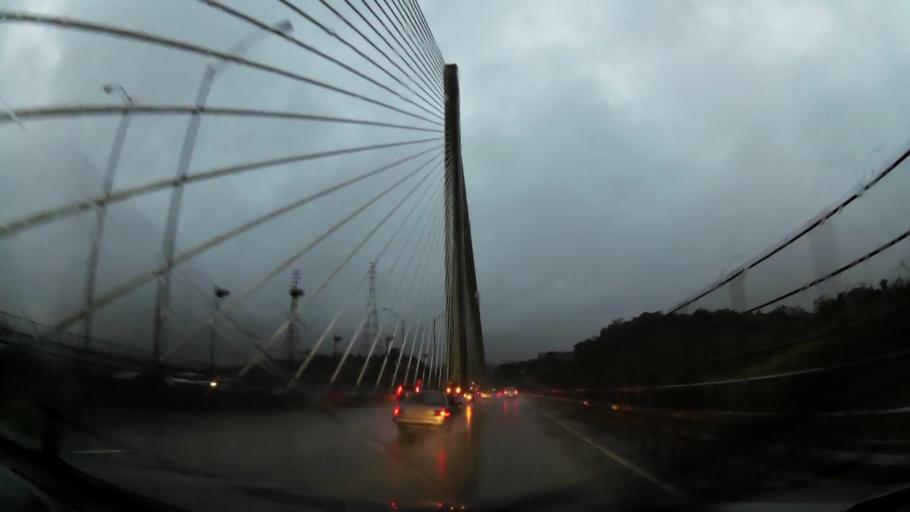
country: PA
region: Panama
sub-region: Distrito de Panama
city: Paraiso
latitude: 9.0308
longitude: -79.6356
